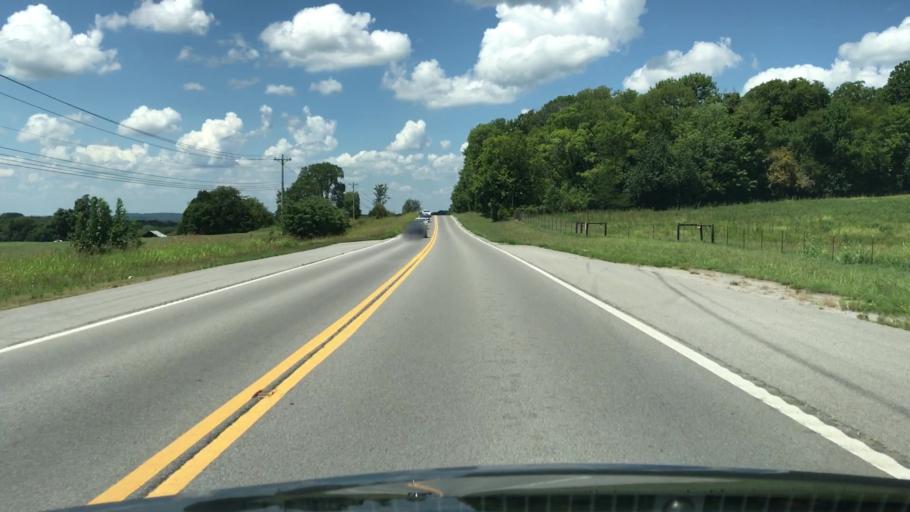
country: US
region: Tennessee
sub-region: Williamson County
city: Nolensville
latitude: 35.8514
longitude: -86.6195
